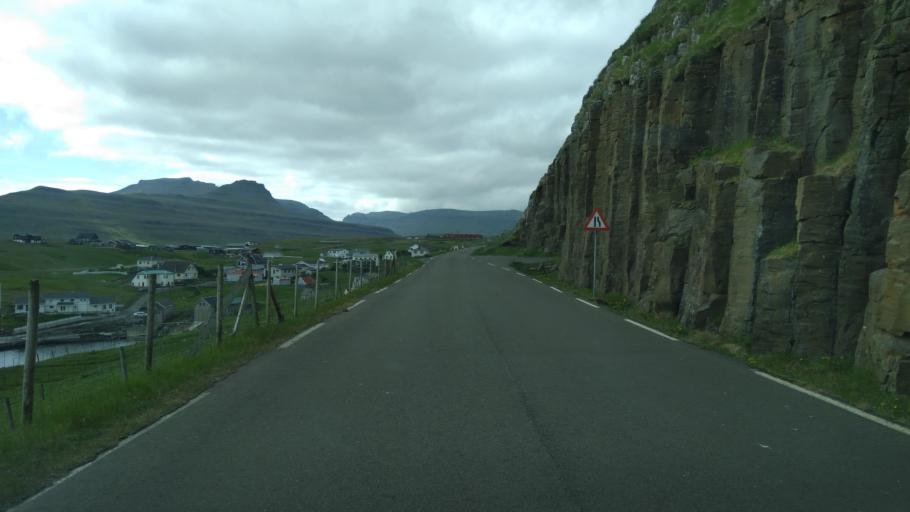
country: FO
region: Suduroy
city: Tvoroyri
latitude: 61.5459
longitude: -6.7687
